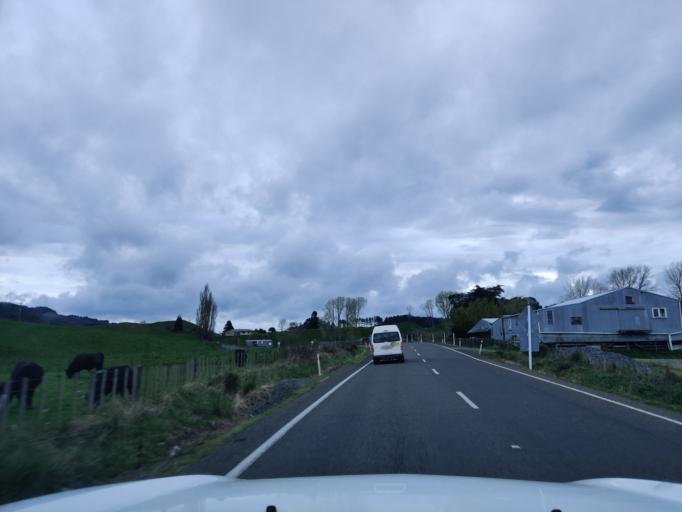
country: NZ
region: Waikato
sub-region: Otorohanga District
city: Otorohanga
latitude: -38.4487
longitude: 175.1599
